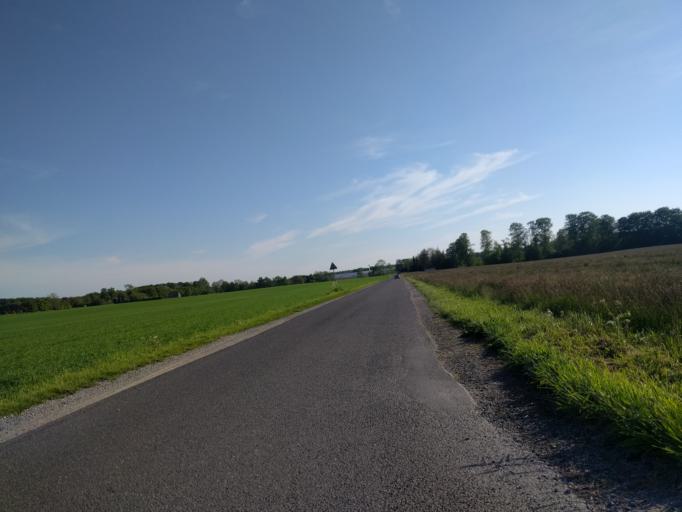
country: DK
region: South Denmark
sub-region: Kerteminde Kommune
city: Munkebo
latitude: 55.4092
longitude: 10.5622
